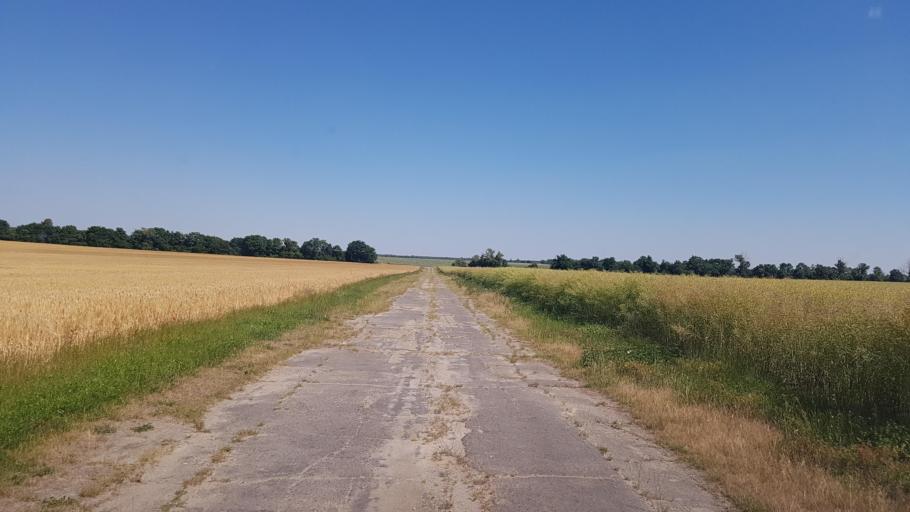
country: DE
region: Saxony-Anhalt
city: Seyda
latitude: 51.9645
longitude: 12.8946
